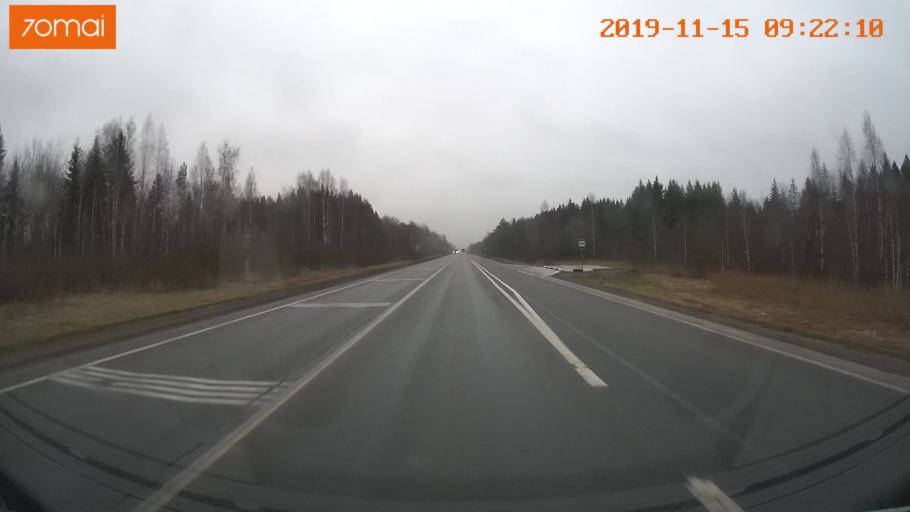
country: RU
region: Vologda
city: Tonshalovo
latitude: 59.2970
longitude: 38.0831
